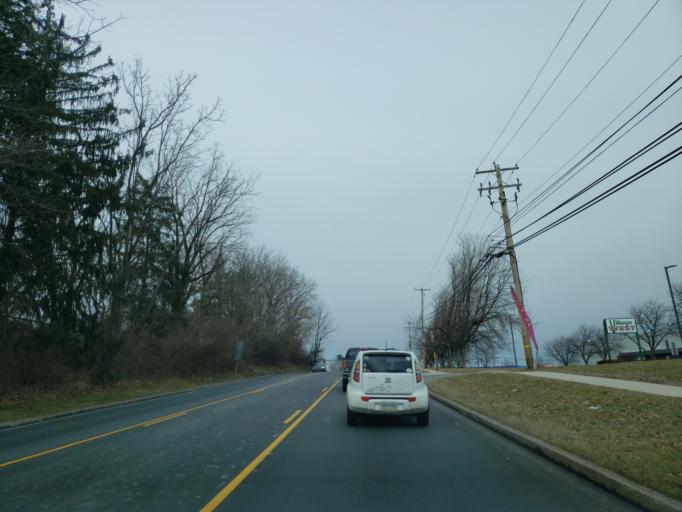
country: US
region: Pennsylvania
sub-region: Lehigh County
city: Dorneyville
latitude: 40.5960
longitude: -75.5273
